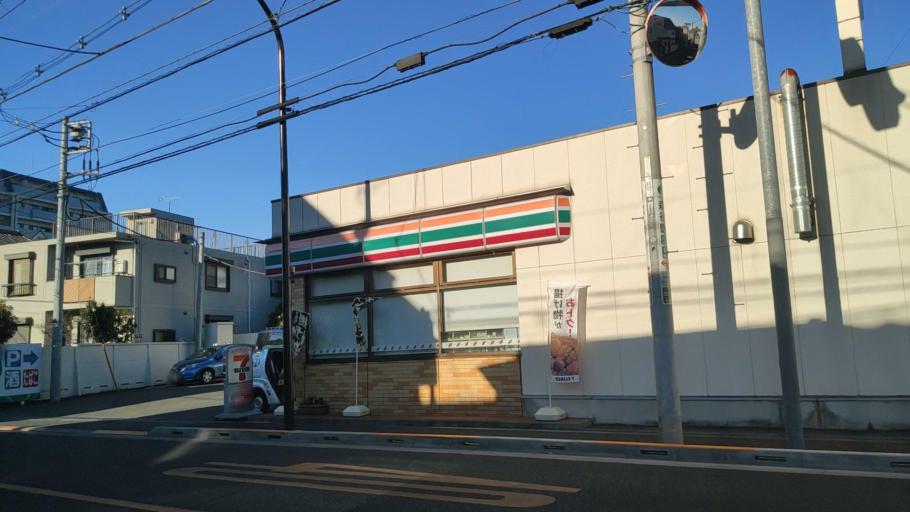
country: JP
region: Tokyo
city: Musashino
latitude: 35.6974
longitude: 139.5991
